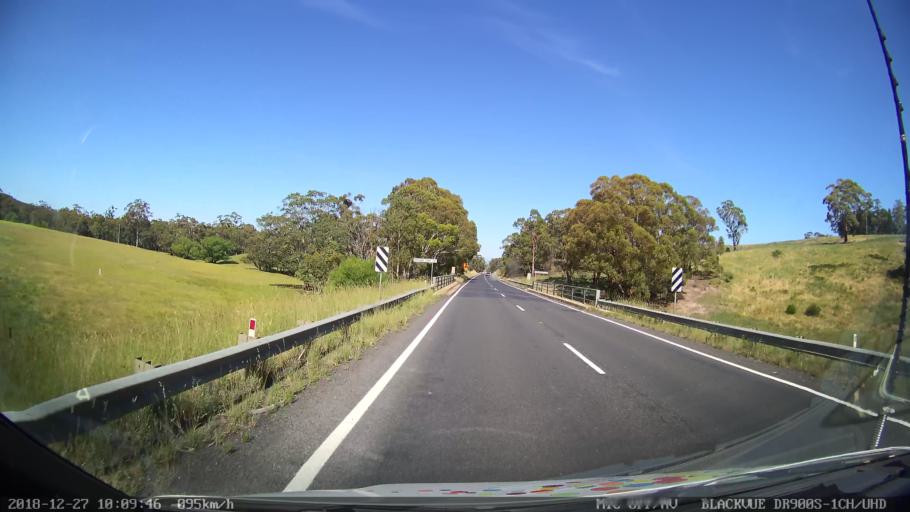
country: AU
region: New South Wales
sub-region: Lithgow
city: Portland
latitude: -33.4518
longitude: 149.8032
